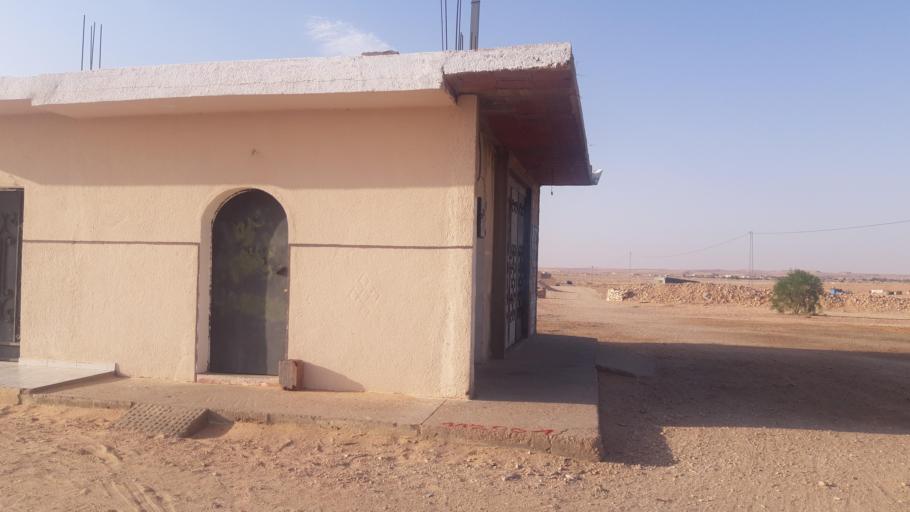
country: TN
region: Tataouine
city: Remada
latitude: 32.3363
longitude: 10.3582
